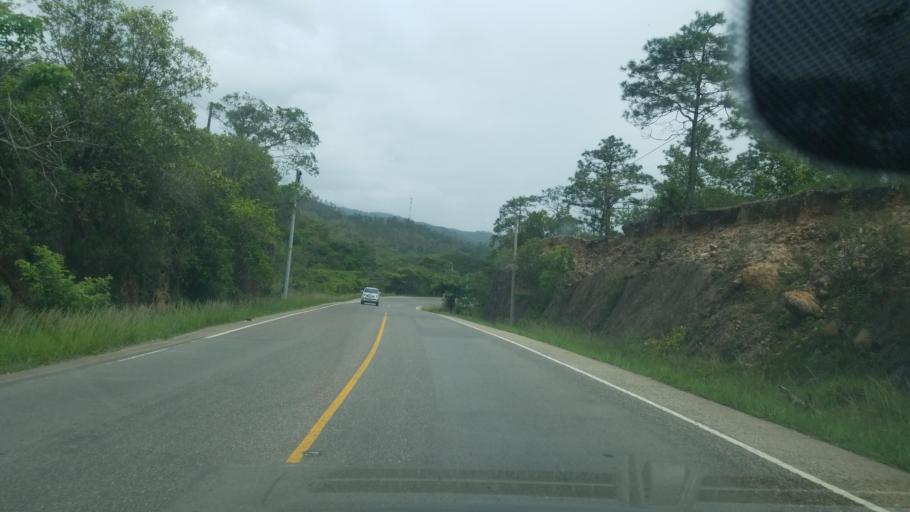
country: HN
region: Ocotepeque
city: Lucerna
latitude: 14.5770
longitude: -88.9305
